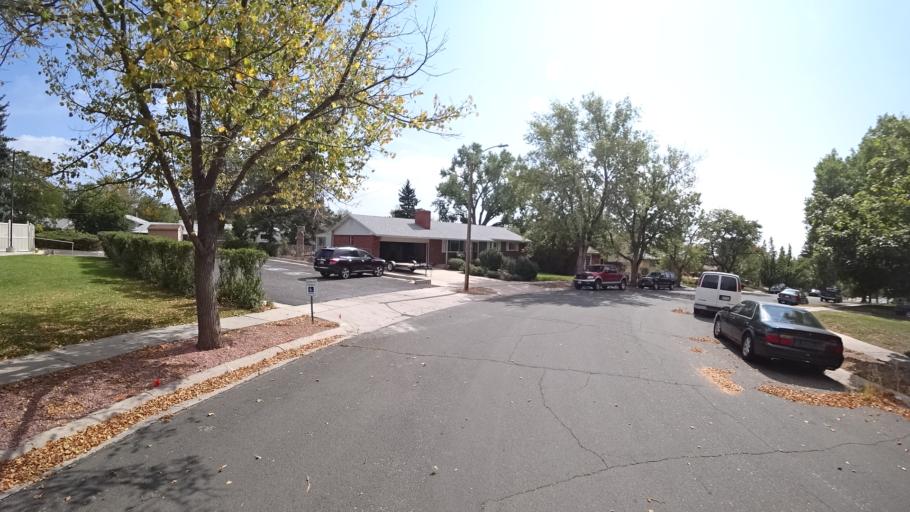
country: US
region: Colorado
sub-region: El Paso County
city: Colorado Springs
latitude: 38.8632
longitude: -104.7672
